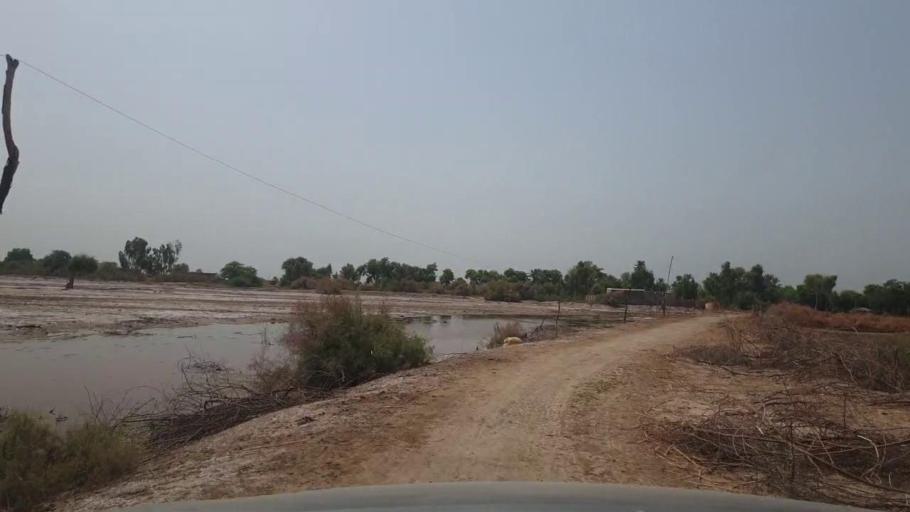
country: PK
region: Sindh
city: Garhi Yasin
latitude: 27.9543
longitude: 68.3841
